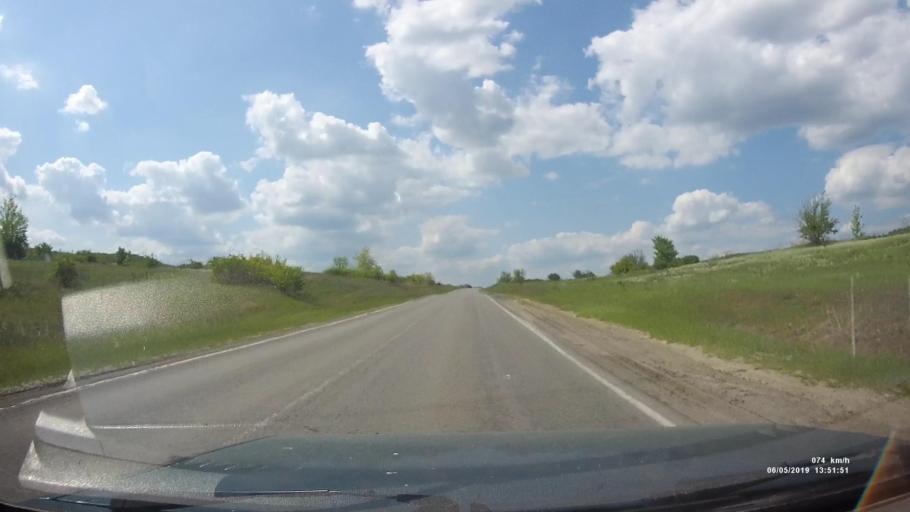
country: RU
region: Rostov
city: Melikhovskaya
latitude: 47.6587
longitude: 40.4857
